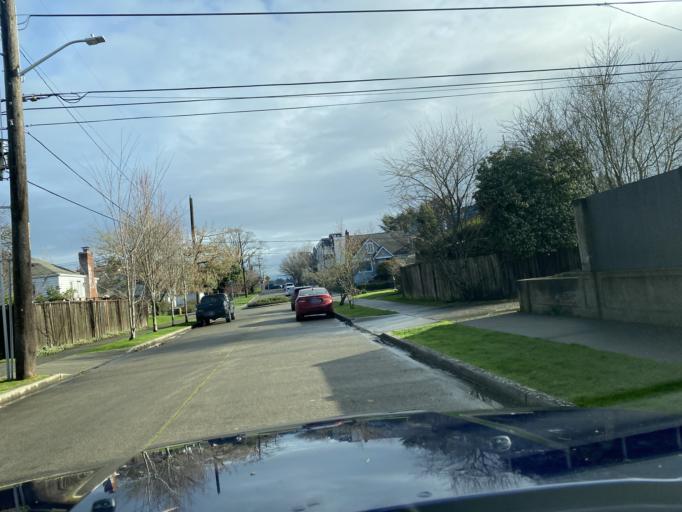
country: US
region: Washington
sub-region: King County
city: Medina
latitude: 47.6370
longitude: -122.2805
